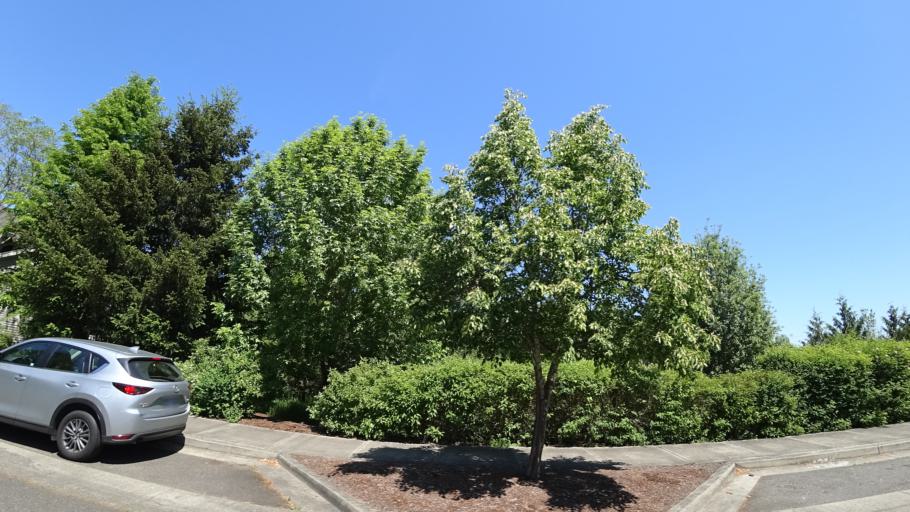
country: US
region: Oregon
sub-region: Washington County
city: Aloha
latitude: 45.4937
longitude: -122.8421
